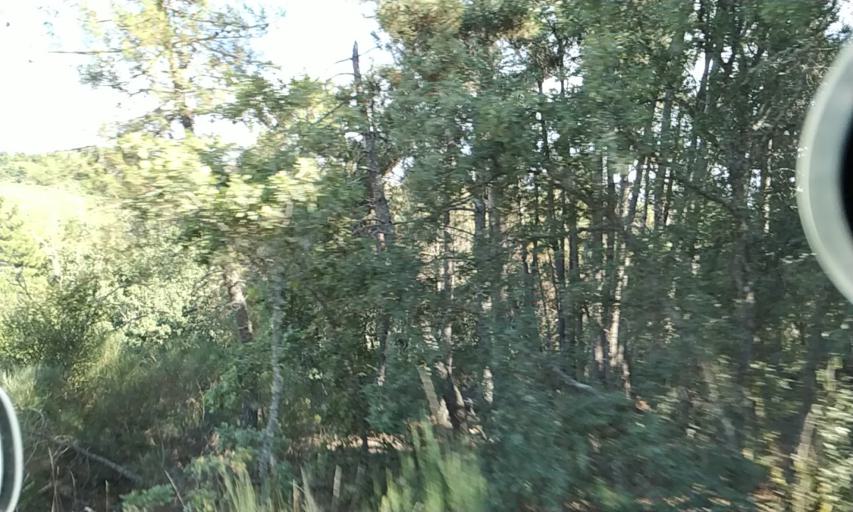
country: PT
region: Vila Real
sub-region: Murca
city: Murca
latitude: 41.3701
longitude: -7.5358
